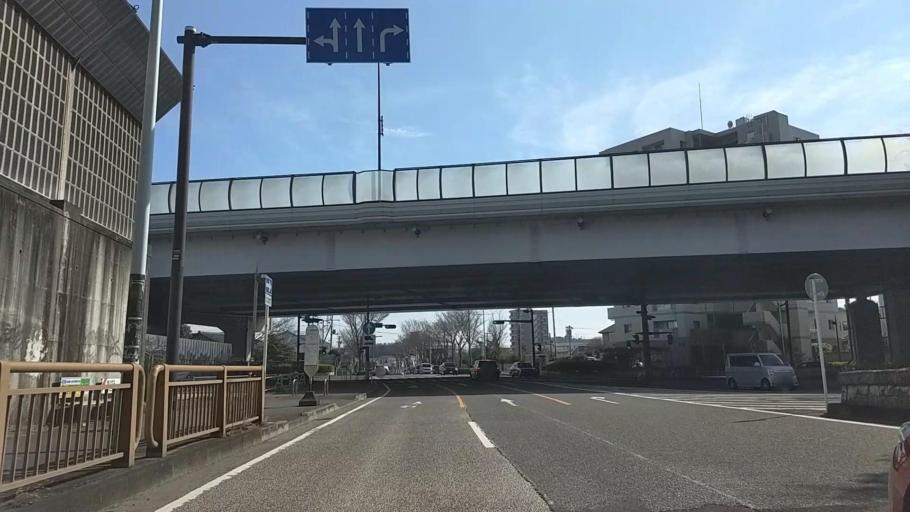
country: JP
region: Kanagawa
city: Fujisawa
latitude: 35.3482
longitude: 139.4471
